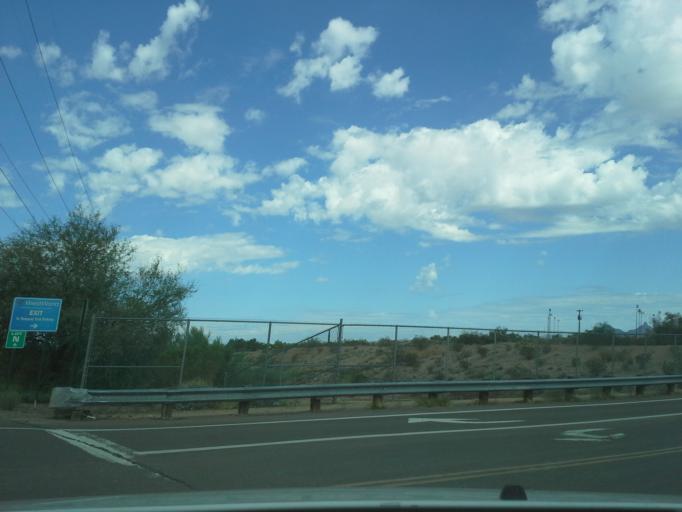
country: US
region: Arizona
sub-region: Maricopa County
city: Paradise Valley
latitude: 33.6302
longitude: -111.8715
